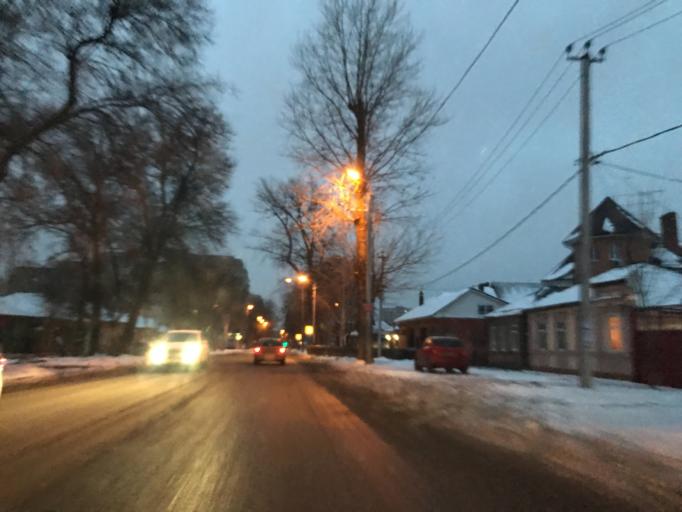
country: RU
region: Rostov
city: Imeni Chkalova
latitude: 47.2485
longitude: 39.7733
